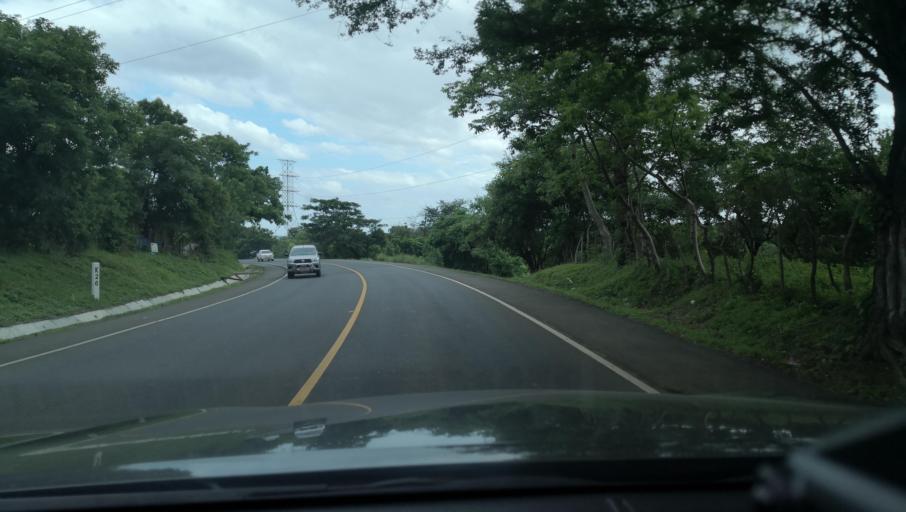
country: NI
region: Masaya
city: Nindiri
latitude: 12.0563
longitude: -86.1364
